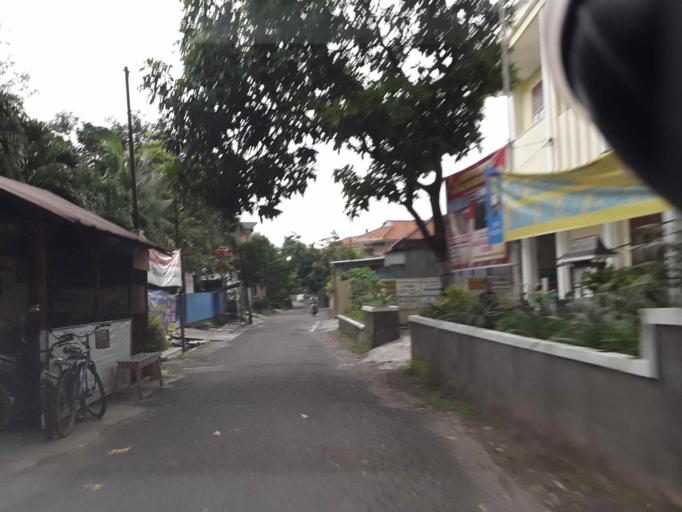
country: ID
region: Central Java
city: Surakarta
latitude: -7.5533
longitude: 110.8148
